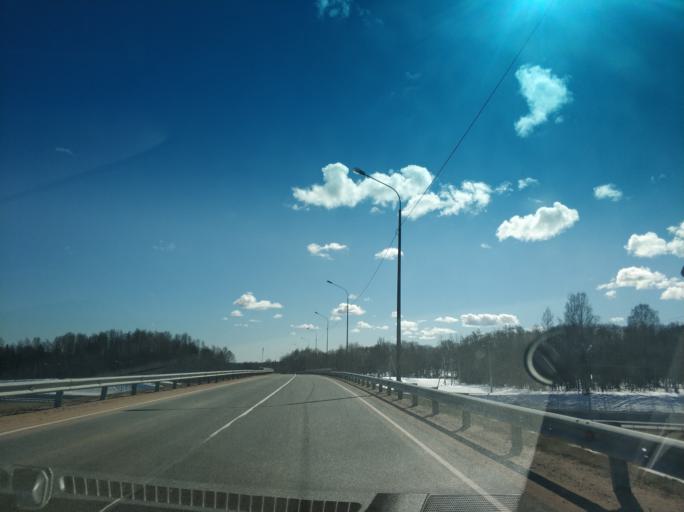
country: RU
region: Leningrad
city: Sosnovo
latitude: 60.4347
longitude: 30.2358
